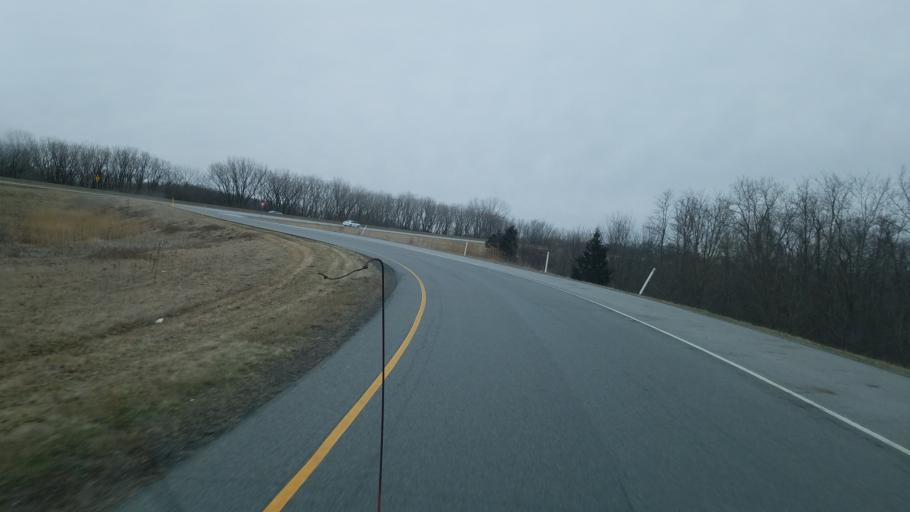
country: US
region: Indiana
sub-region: Porter County
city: Chesterton
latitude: 41.6231
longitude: -87.0470
